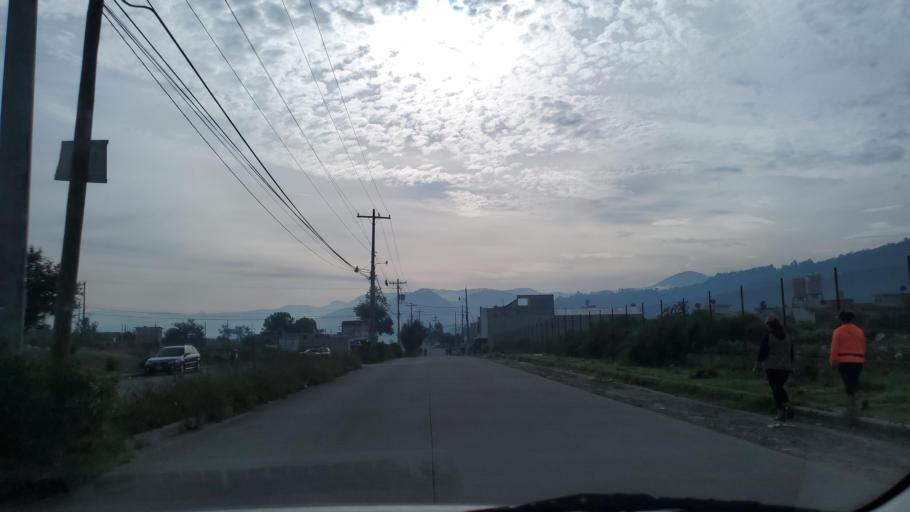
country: GT
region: Quetzaltenango
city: Quetzaltenango
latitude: 14.8323
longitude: -91.5418
